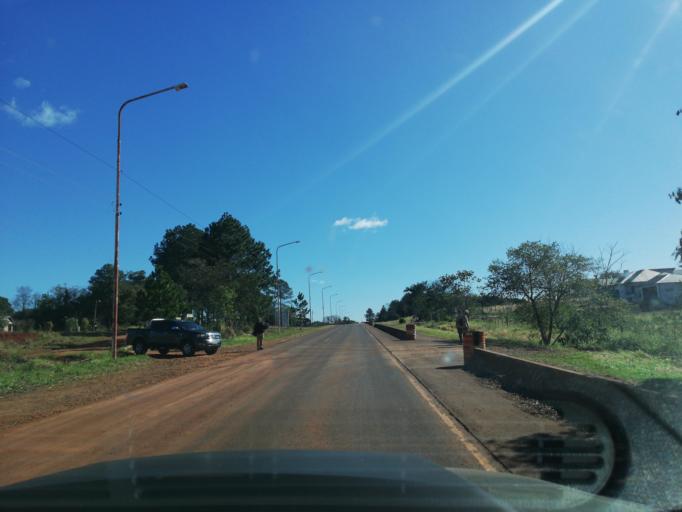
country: AR
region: Misiones
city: Aristobulo del Valle
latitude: -27.0900
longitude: -54.9108
